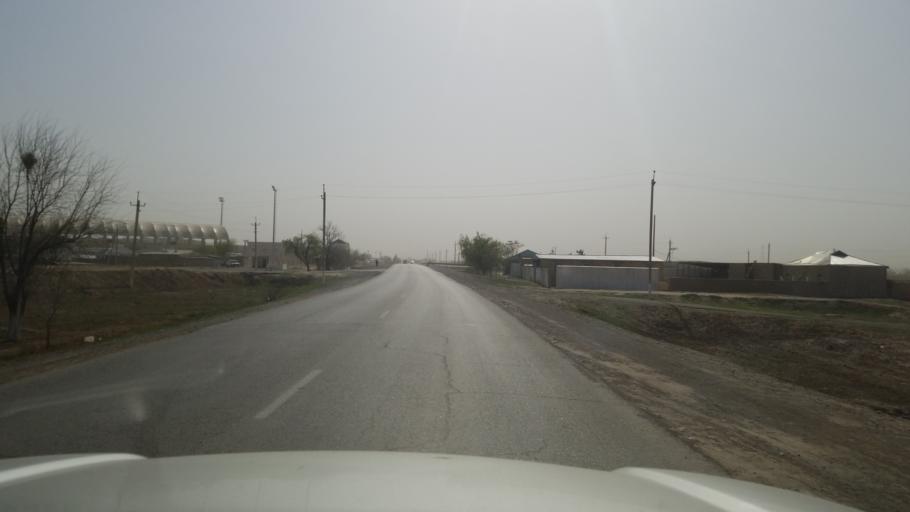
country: TM
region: Mary
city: Yoloeten
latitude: 37.2925
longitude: 62.3378
